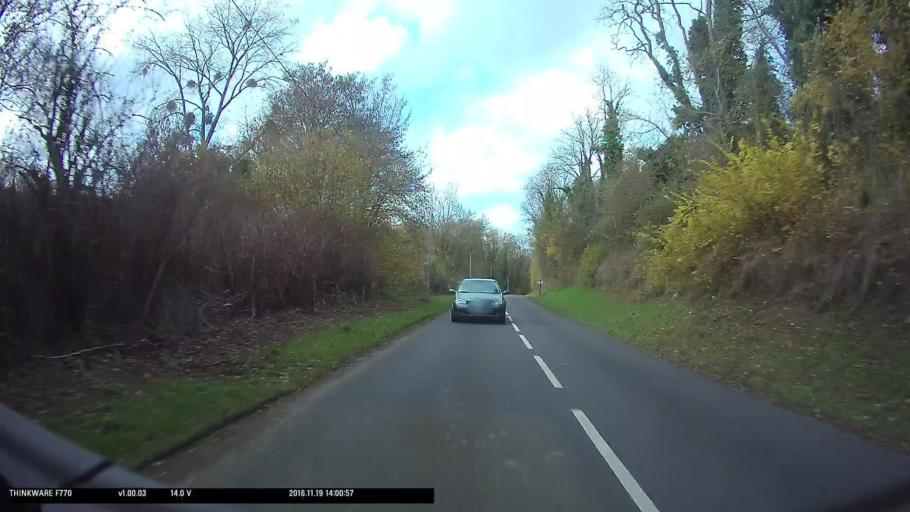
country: FR
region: Ile-de-France
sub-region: Departement du Val-d'Oise
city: Ableiges
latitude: 49.0837
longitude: 1.9999
